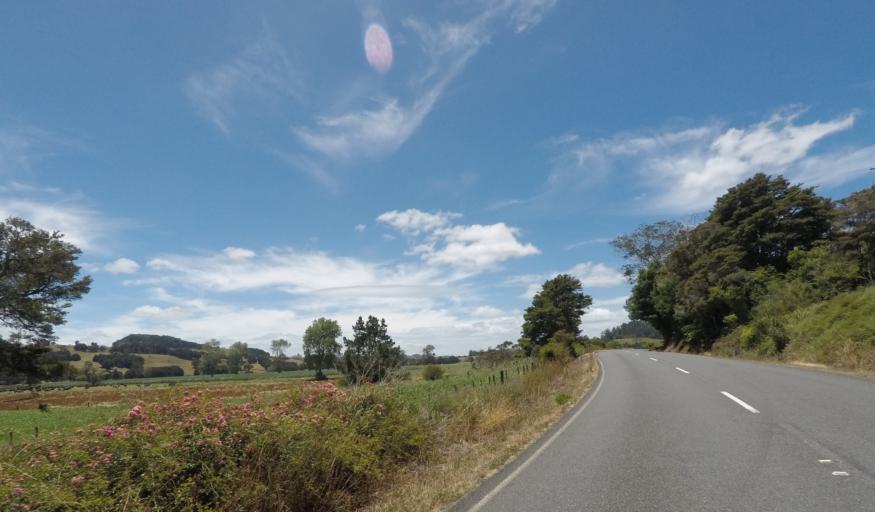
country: NZ
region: Northland
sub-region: Whangarei
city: Whangarei
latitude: -35.5349
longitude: 174.3161
